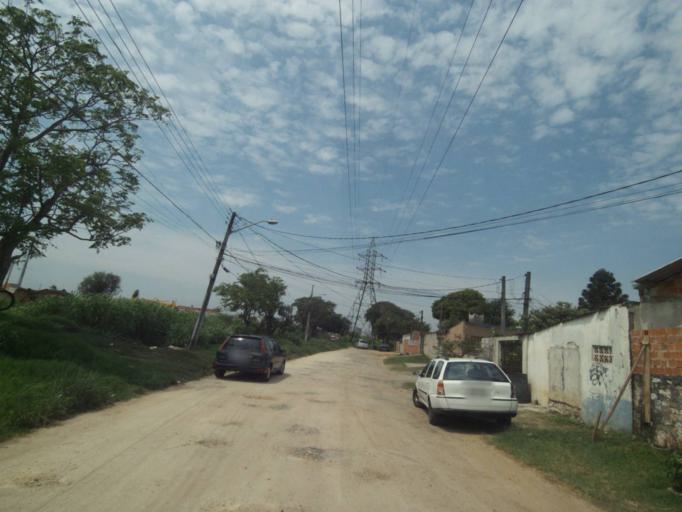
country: BR
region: Parana
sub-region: Pinhais
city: Pinhais
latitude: -25.4243
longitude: -49.1982
